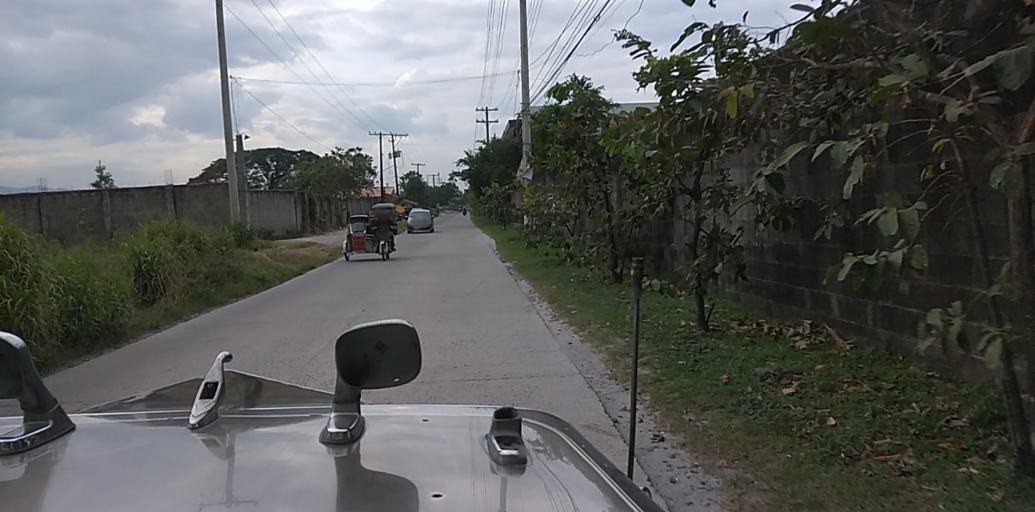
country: PH
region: Central Luzon
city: Santol
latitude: 15.1646
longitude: 120.5472
